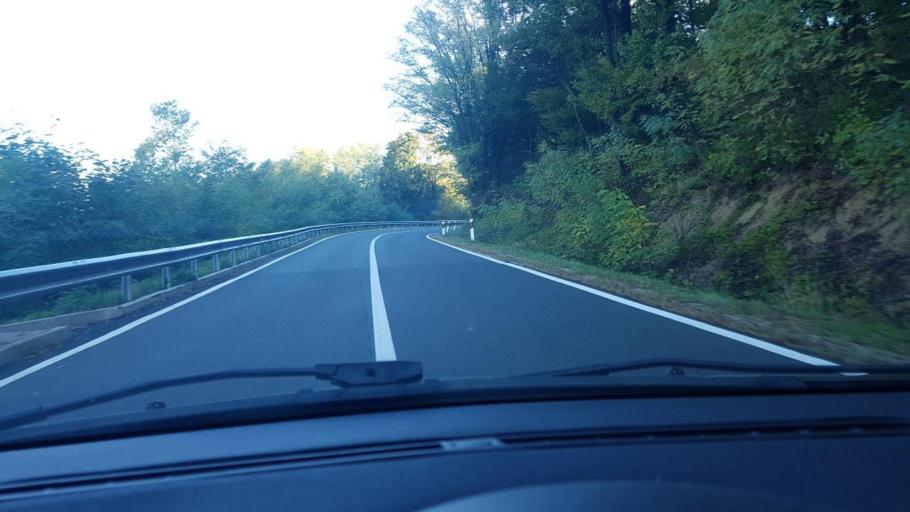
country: HR
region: Krapinsko-Zagorska
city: Marija Bistrica
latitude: 45.9497
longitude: 16.0986
